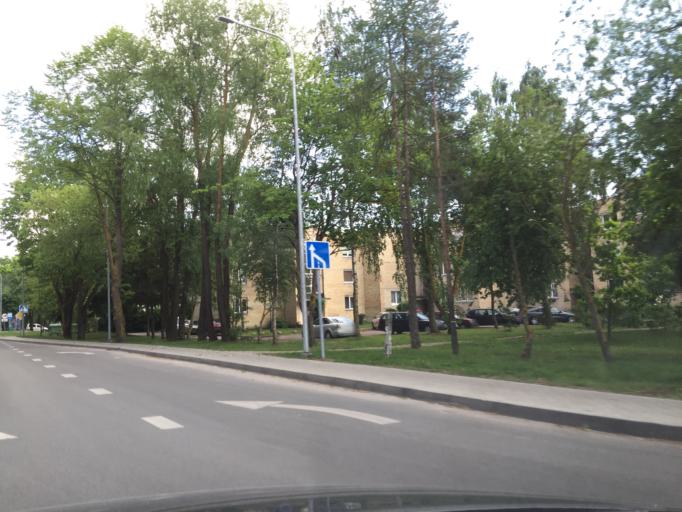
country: LT
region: Klaipedos apskritis
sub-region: Klaipeda
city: Palanga
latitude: 55.9147
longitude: 21.0797
